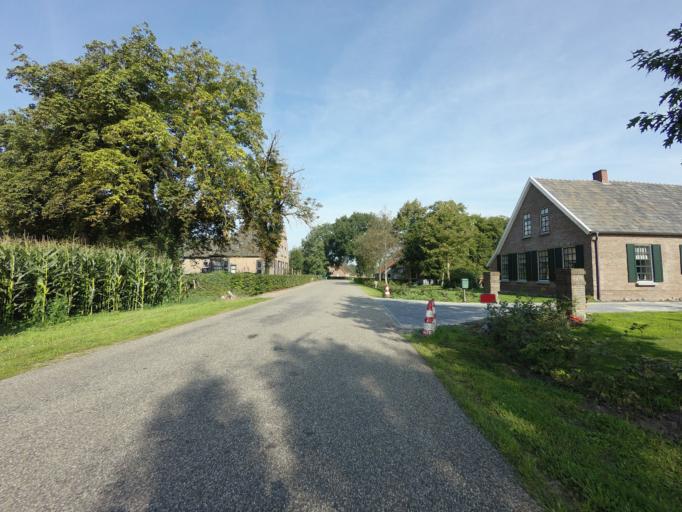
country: DE
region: Lower Saxony
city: Wielen
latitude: 52.5565
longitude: 6.6783
